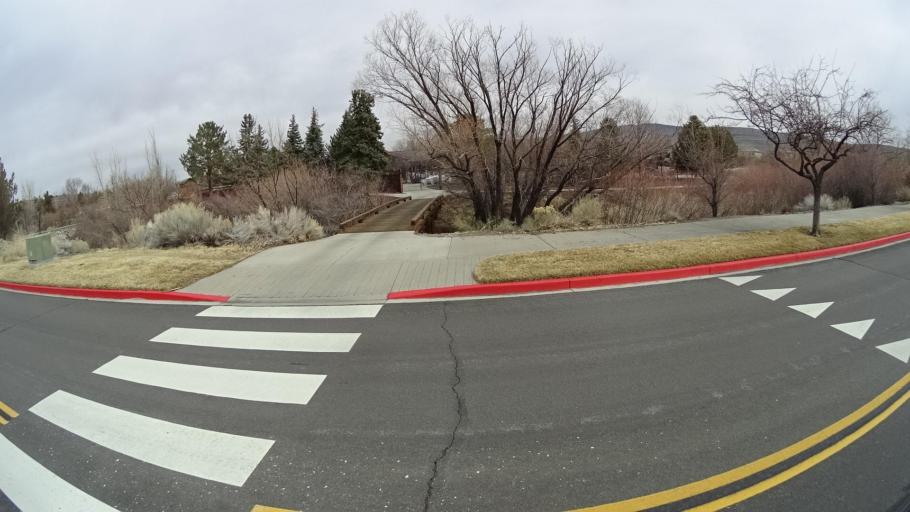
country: US
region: Nevada
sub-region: Washoe County
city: Spanish Springs
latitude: 39.6113
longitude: -119.6892
